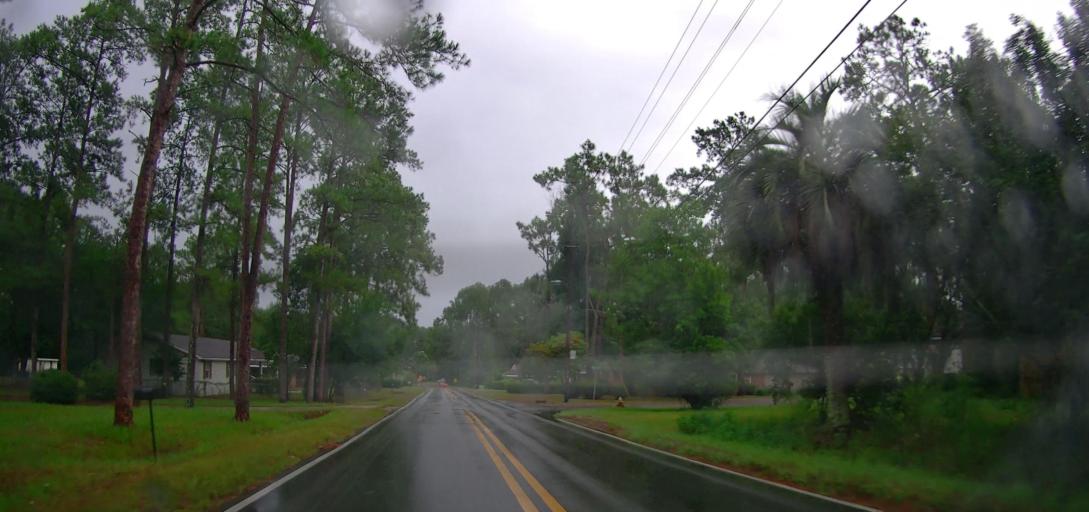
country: US
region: Georgia
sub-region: Ware County
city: Sunnyside
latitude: 31.2264
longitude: -82.3288
